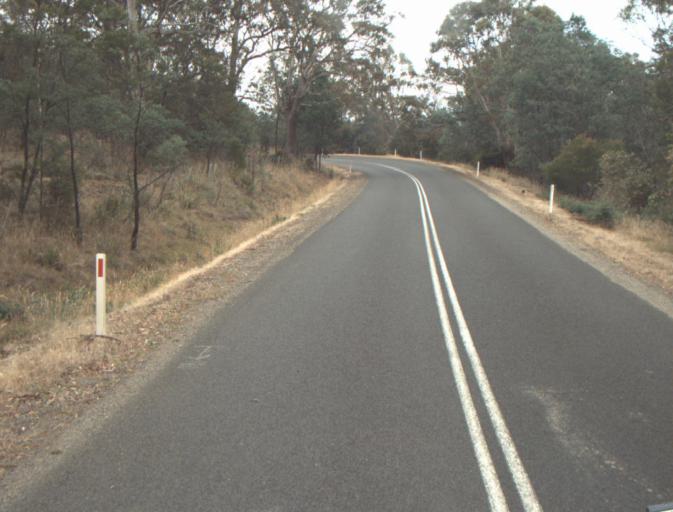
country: AU
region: Tasmania
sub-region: Northern Midlands
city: Evandale
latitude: -41.5009
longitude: 147.3821
